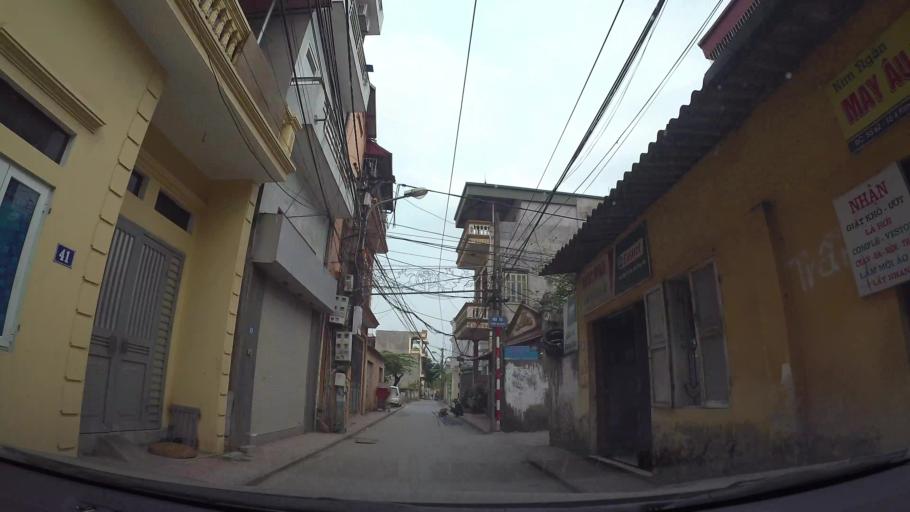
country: VN
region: Ha Noi
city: Trau Quy
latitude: 21.0594
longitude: 105.8995
